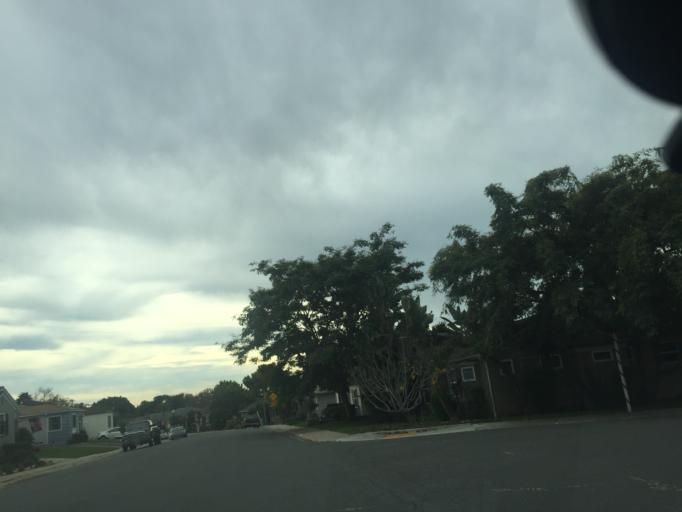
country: US
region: California
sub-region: San Diego County
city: Lemon Grove
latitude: 32.7645
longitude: -117.0898
